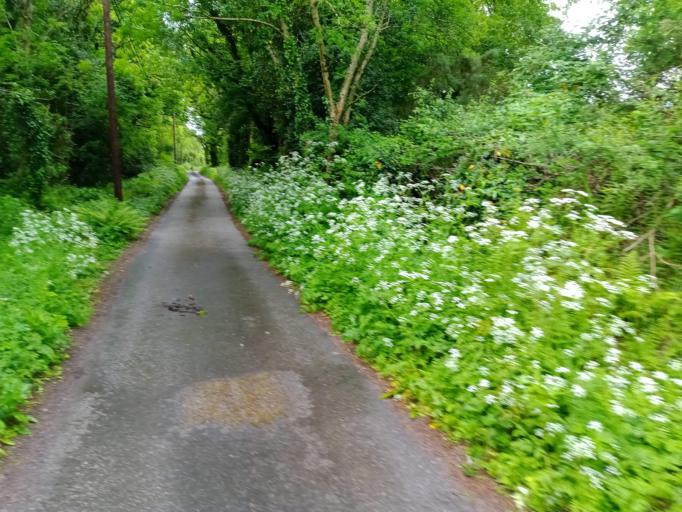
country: IE
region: Leinster
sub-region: Kilkenny
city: Thomastown
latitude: 52.5122
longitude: -7.1323
